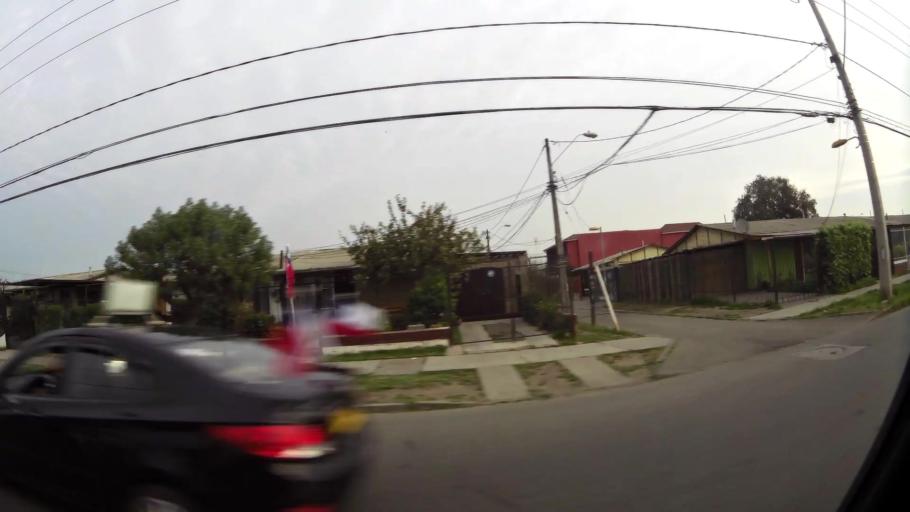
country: CL
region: Santiago Metropolitan
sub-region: Provincia de Santiago
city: Lo Prado
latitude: -33.5220
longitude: -70.7853
